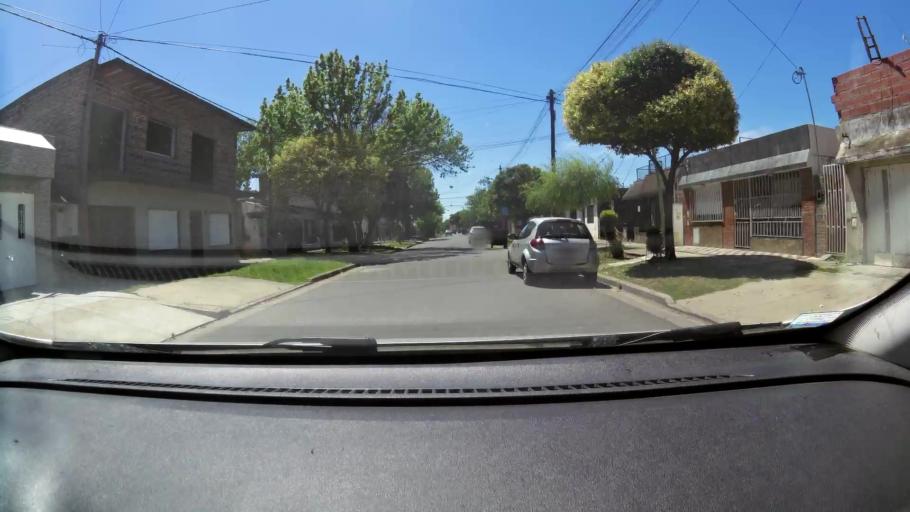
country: AR
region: Santa Fe
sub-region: Departamento de Rosario
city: Rosario
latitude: -32.9557
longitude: -60.7093
